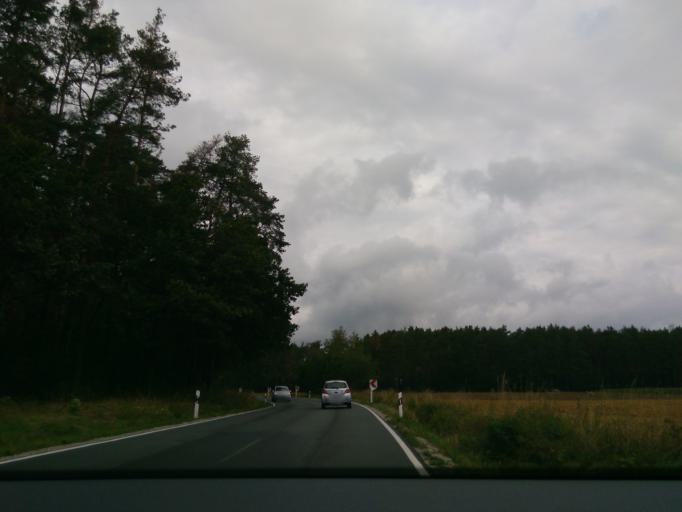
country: DE
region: Bavaria
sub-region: Regierungsbezirk Mittelfranken
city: Weisendorf
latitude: 49.6491
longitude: 10.8155
